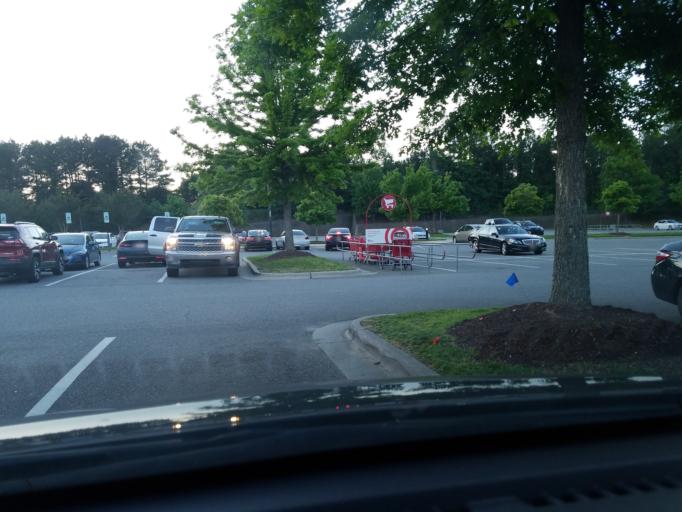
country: US
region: North Carolina
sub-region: Orange County
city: Chapel Hill
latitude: 35.9031
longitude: -78.9556
